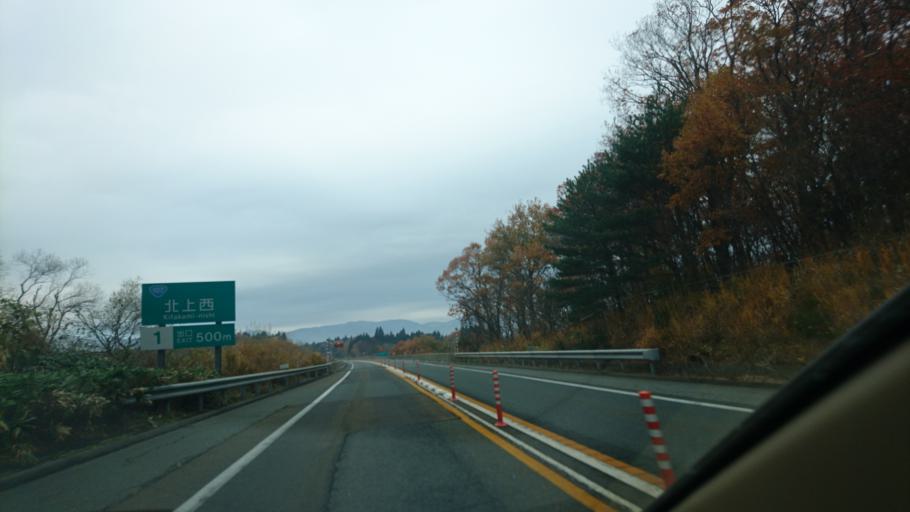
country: JP
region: Iwate
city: Kitakami
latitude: 39.2878
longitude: 140.9924
